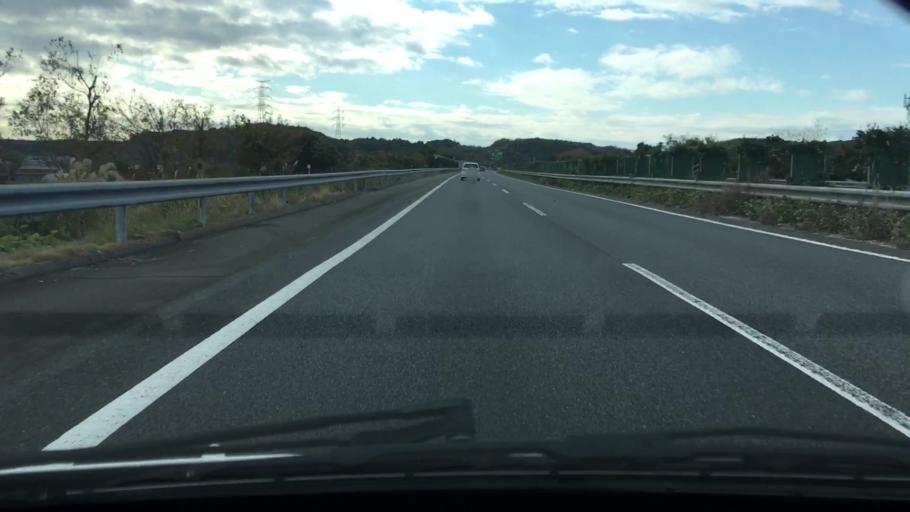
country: JP
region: Chiba
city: Kisarazu
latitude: 35.3977
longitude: 140.0057
